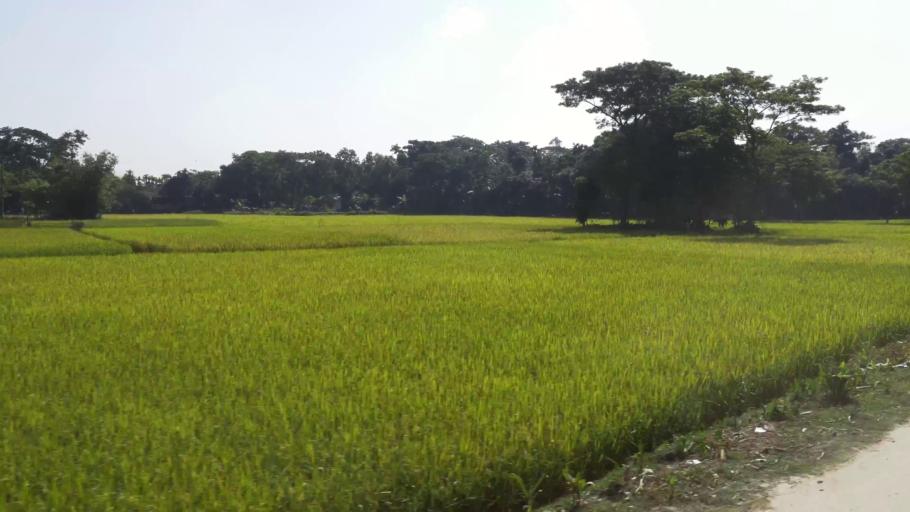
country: BD
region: Dhaka
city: Gafargaon
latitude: 24.4908
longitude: 90.5262
